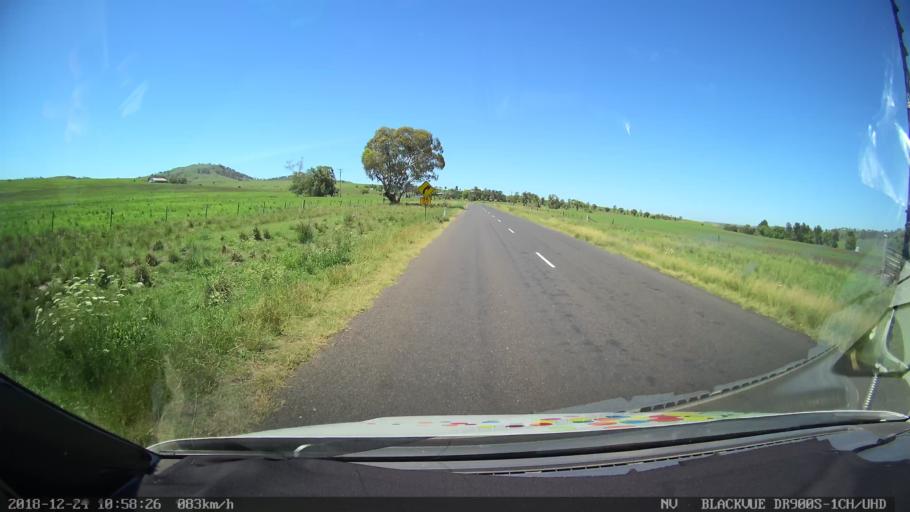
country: AU
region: New South Wales
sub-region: Upper Hunter Shire
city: Merriwa
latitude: -32.0474
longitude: 150.4064
